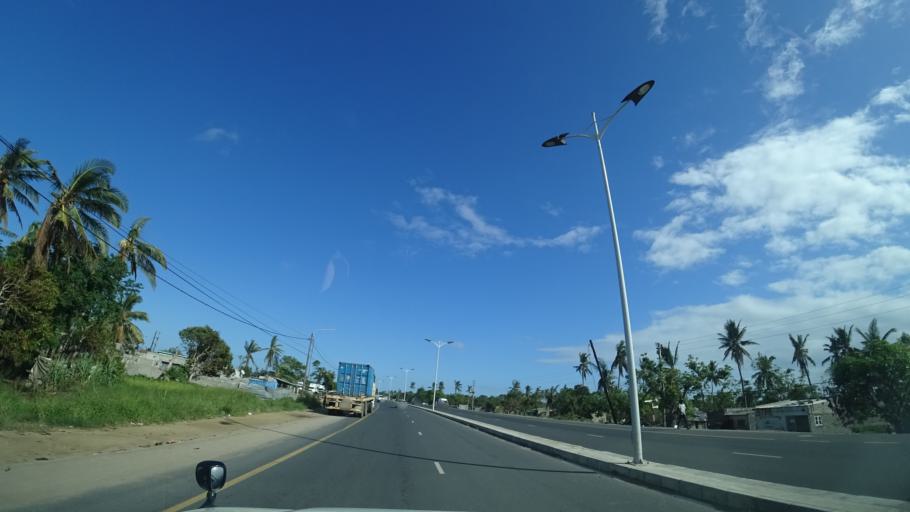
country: MZ
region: Sofala
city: Beira
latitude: -19.7411
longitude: 34.8626
